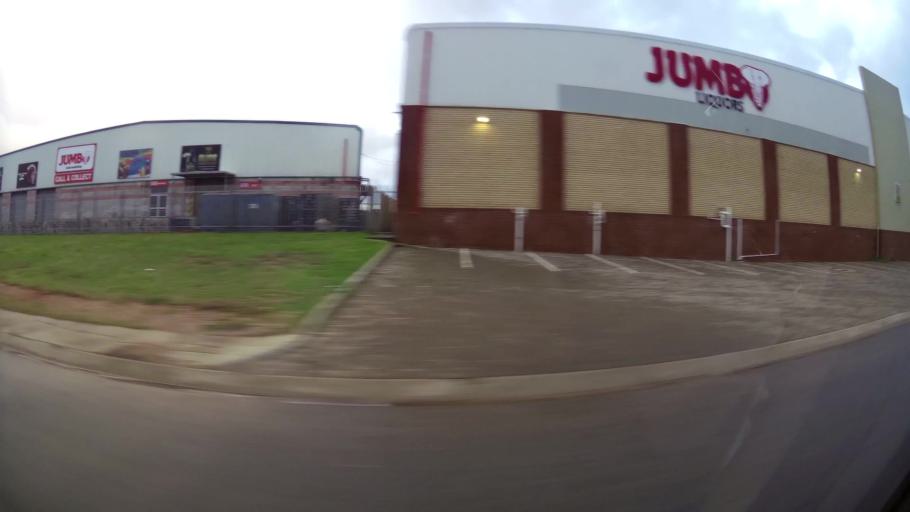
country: ZA
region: Eastern Cape
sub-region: Nelson Mandela Bay Metropolitan Municipality
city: Port Elizabeth
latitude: -33.9298
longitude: 25.6044
